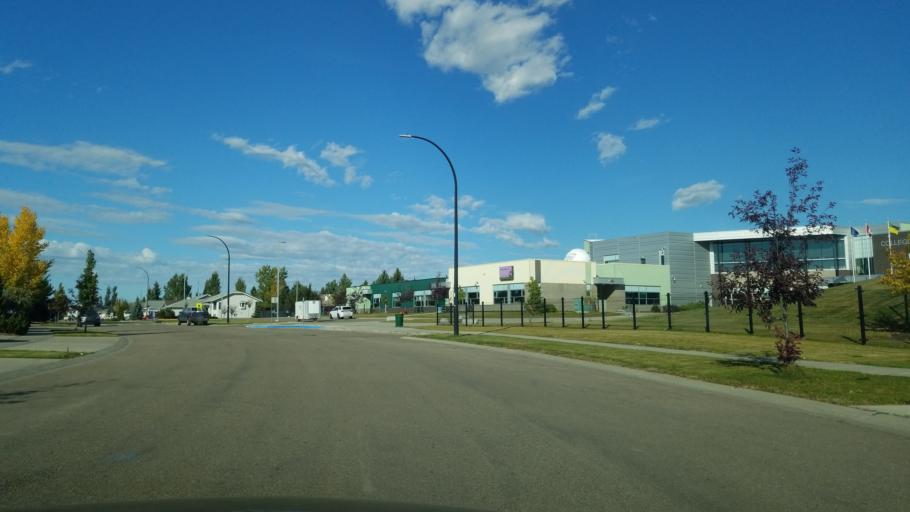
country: CA
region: Saskatchewan
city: Lloydminster
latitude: 53.2554
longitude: -110.0216
